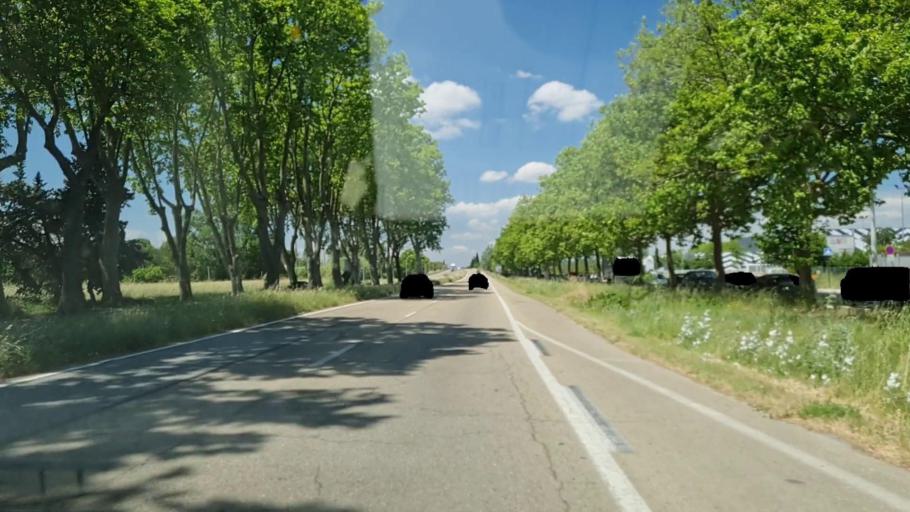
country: FR
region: Languedoc-Roussillon
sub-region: Departement du Gard
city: Rodilhan
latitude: 43.8344
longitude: 4.4142
